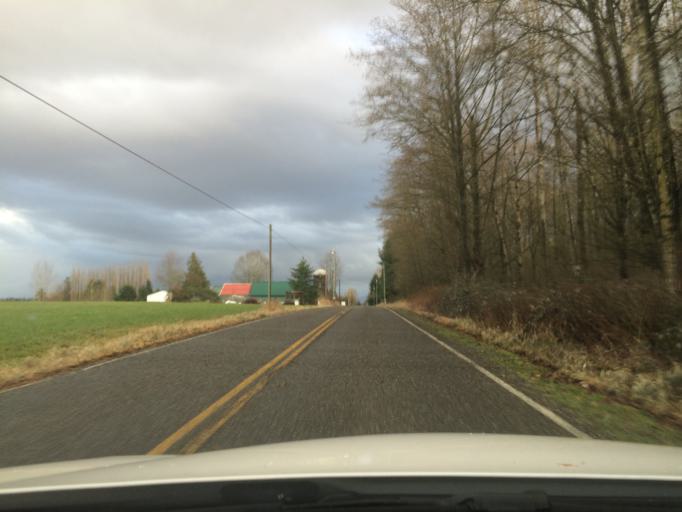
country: CA
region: British Columbia
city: Aldergrove
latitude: 48.9933
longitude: -122.5337
